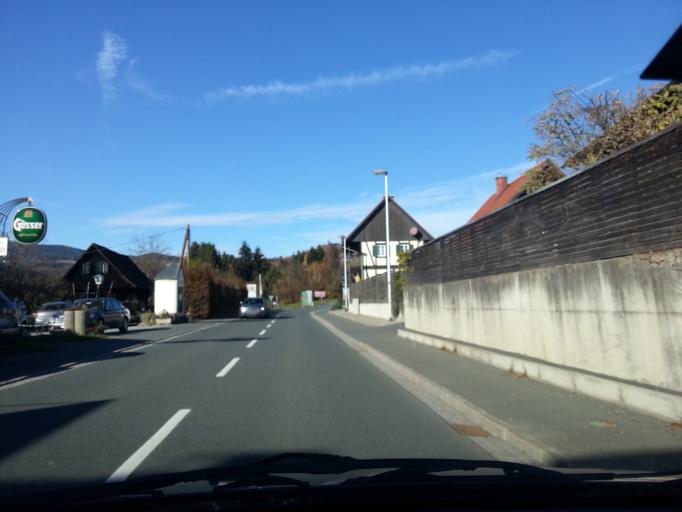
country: AT
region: Styria
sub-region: Politischer Bezirk Deutschlandsberg
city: Sankt Stefan ob Stainz
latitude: 46.9306
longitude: 15.2503
